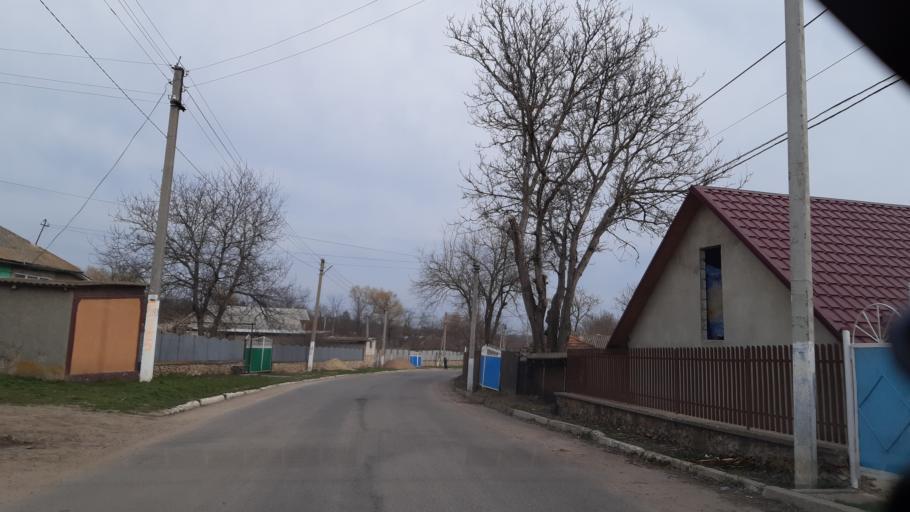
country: MD
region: Soldanesti
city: Soldanesti
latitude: 47.6850
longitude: 28.7568
